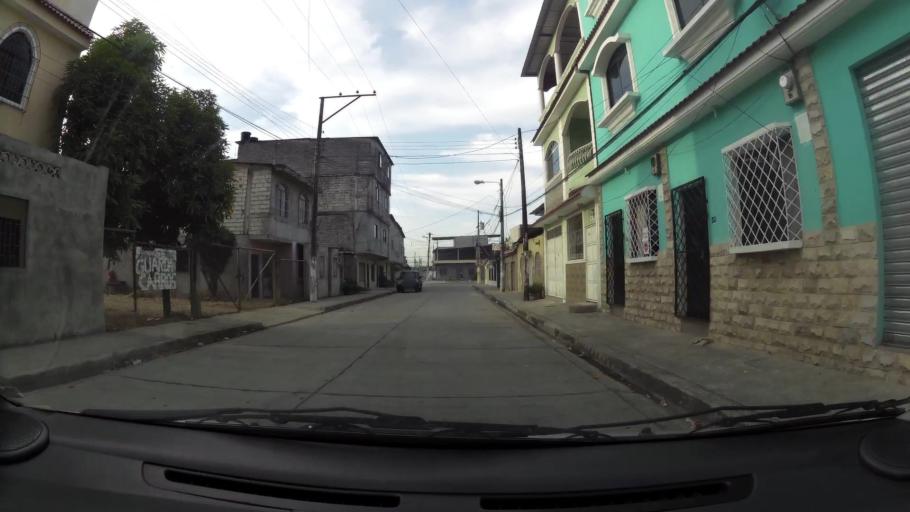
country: EC
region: Guayas
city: Eloy Alfaro
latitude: -2.0931
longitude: -79.9074
